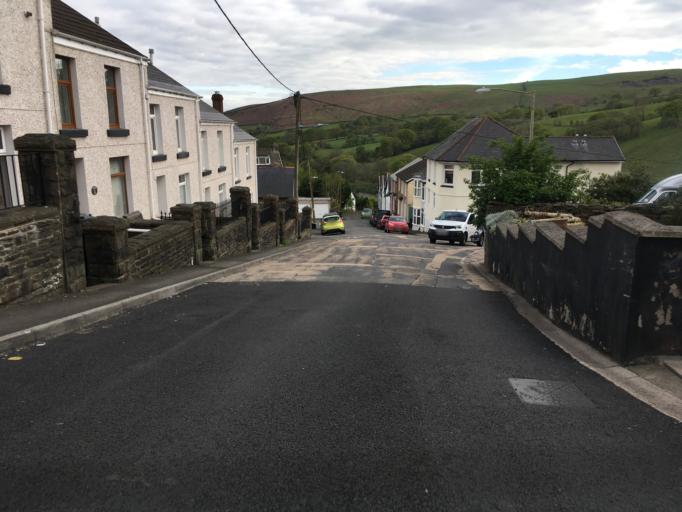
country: GB
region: Wales
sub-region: Merthyr Tydfil County Borough
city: Treharris
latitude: 51.7017
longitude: -3.3112
